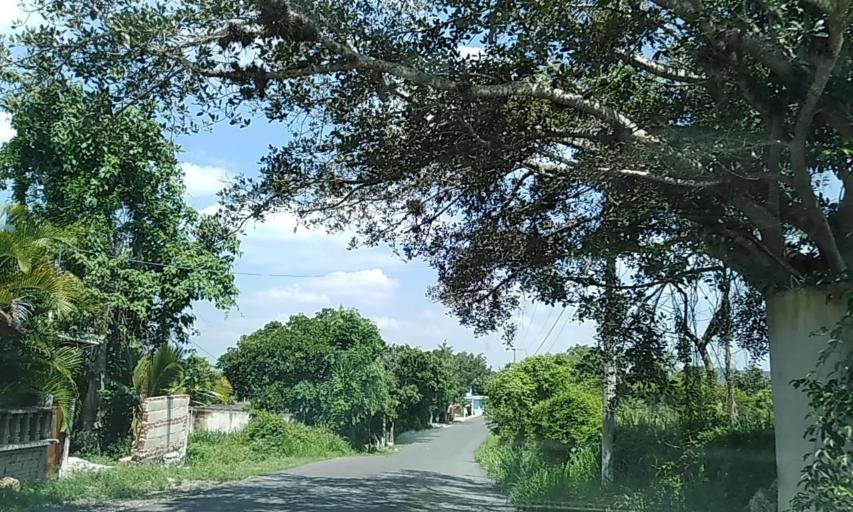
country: MX
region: Veracruz
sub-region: Emiliano Zapata
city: Dos Rios
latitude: 19.4386
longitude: -96.7795
